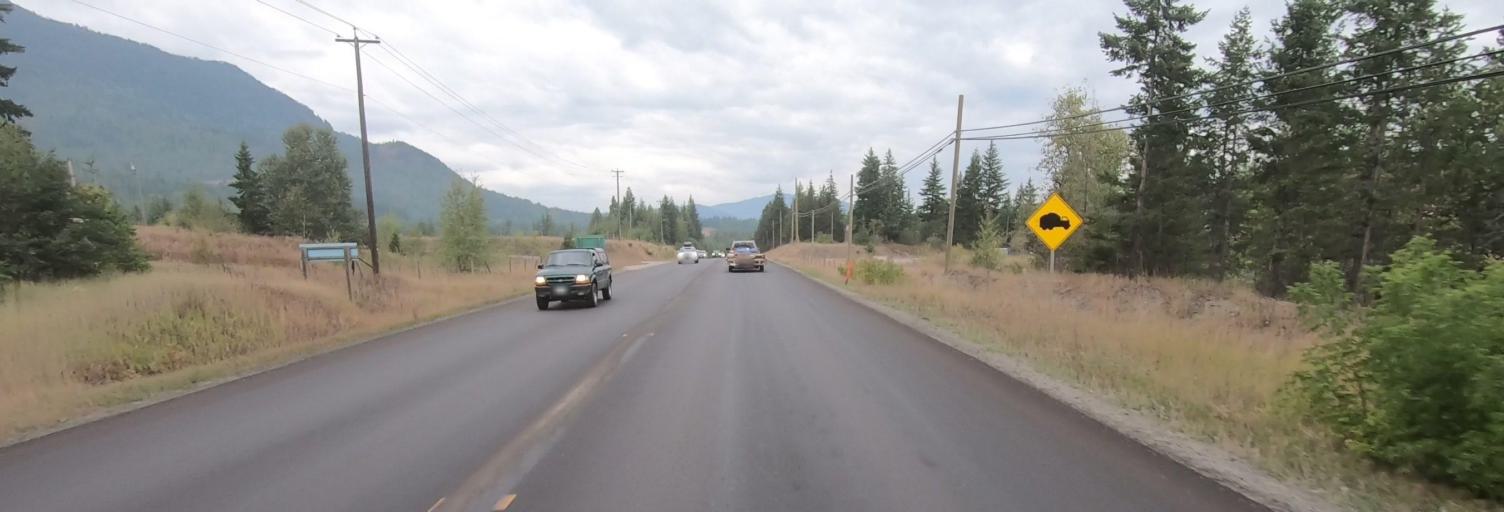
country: CA
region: British Columbia
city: Chase
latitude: 50.8815
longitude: -119.4917
